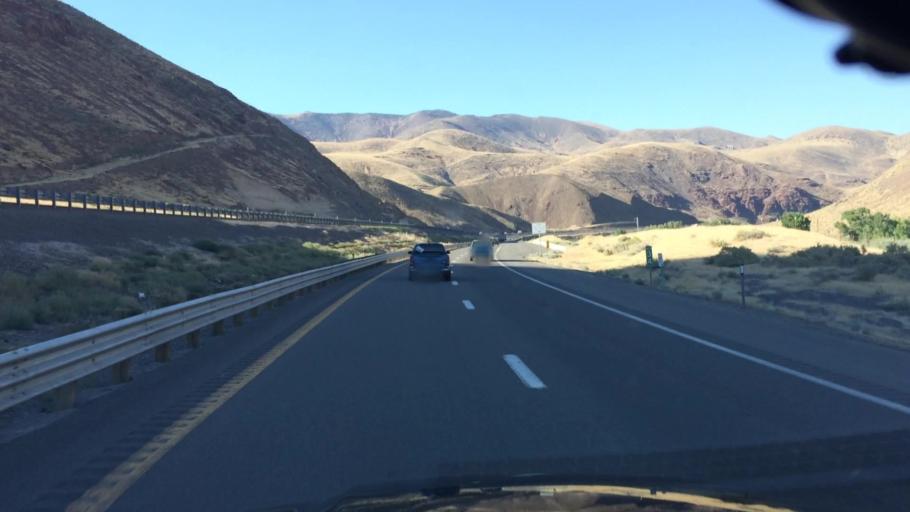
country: US
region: Nevada
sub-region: Lyon County
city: Fernley
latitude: 39.5767
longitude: -119.4721
